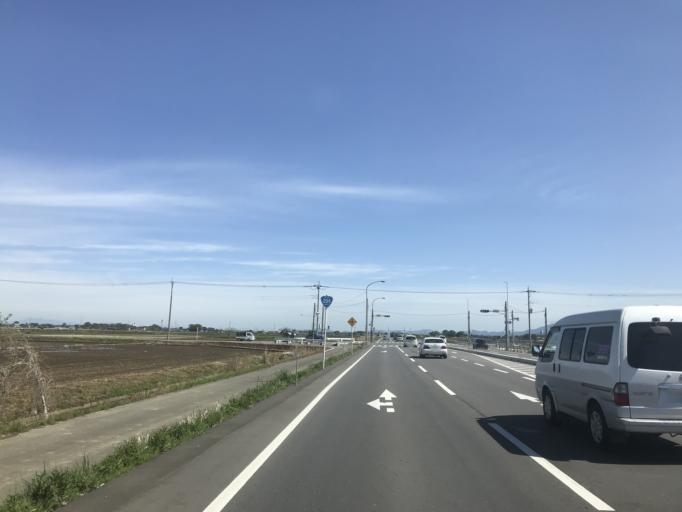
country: JP
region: Ibaraki
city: Ishige
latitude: 36.1316
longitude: 139.9835
